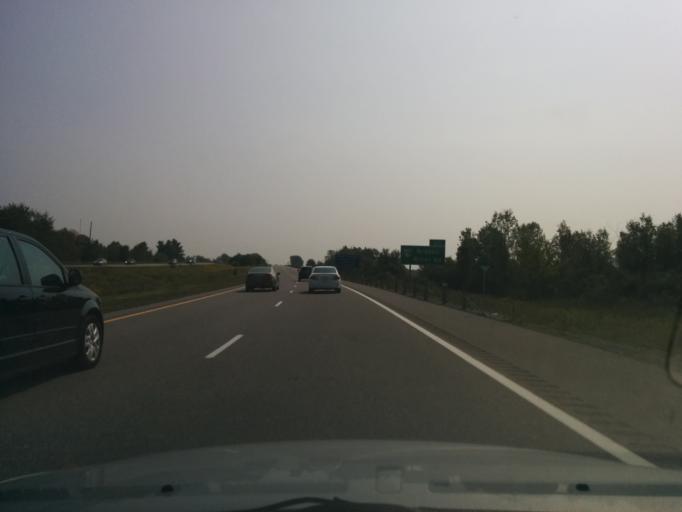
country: CA
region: Ontario
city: Bells Corners
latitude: 45.0847
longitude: -75.6452
